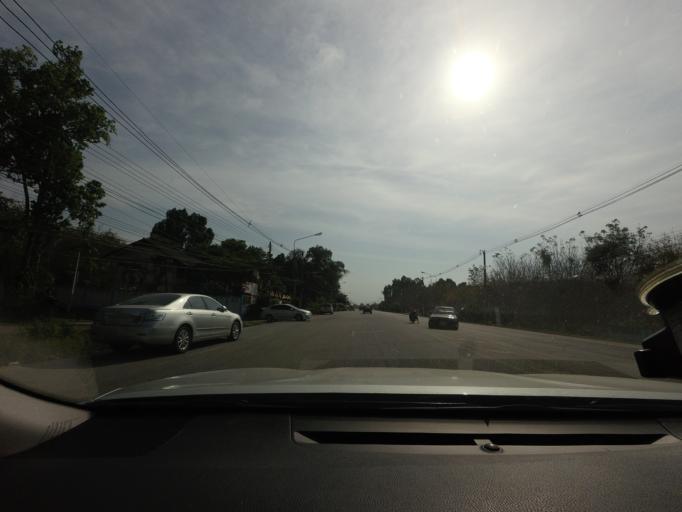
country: TH
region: Narathiwat
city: Narathiwat
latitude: 6.3781
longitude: 101.8008
